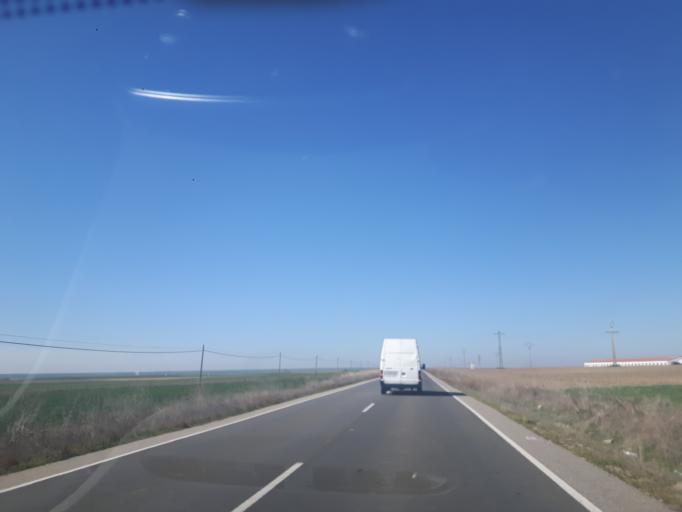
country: ES
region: Castille and Leon
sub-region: Provincia de Salamanca
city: Penaranda de Bracamonte
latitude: 40.8968
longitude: -5.2304
